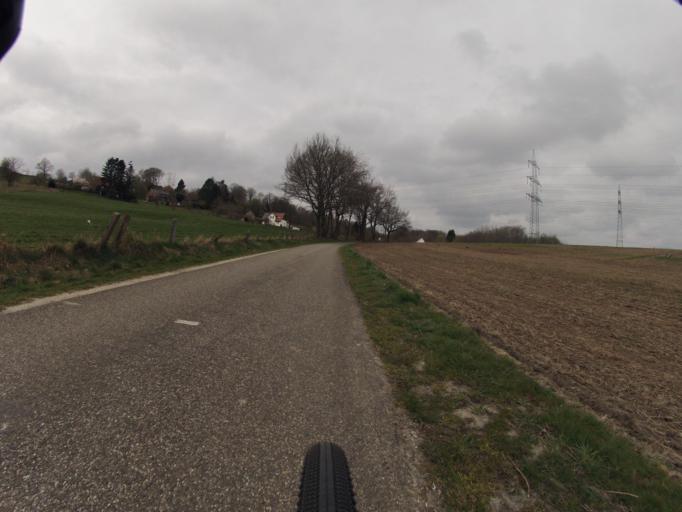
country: DE
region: North Rhine-Westphalia
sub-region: Regierungsbezirk Munster
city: Tecklenburg
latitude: 52.2769
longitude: 7.8312
